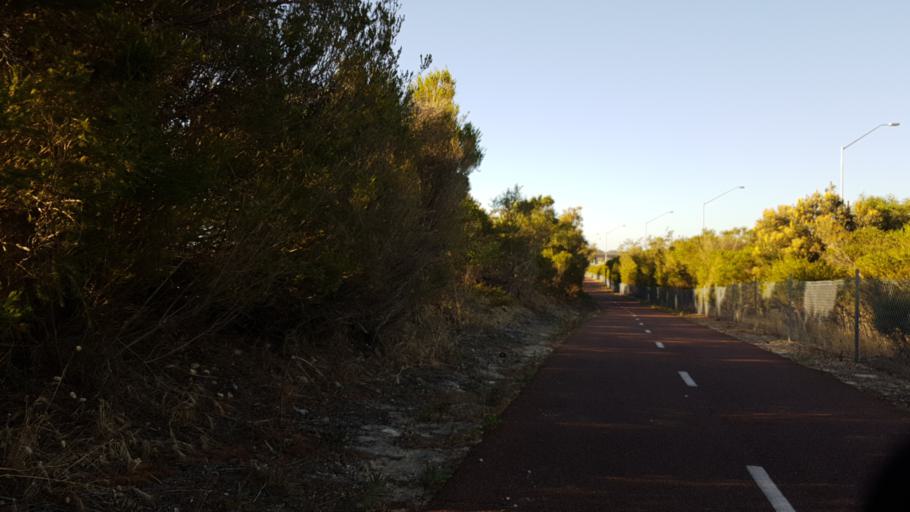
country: AU
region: Western Australia
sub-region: Kwinana
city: Bertram
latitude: -32.2370
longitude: 115.8505
